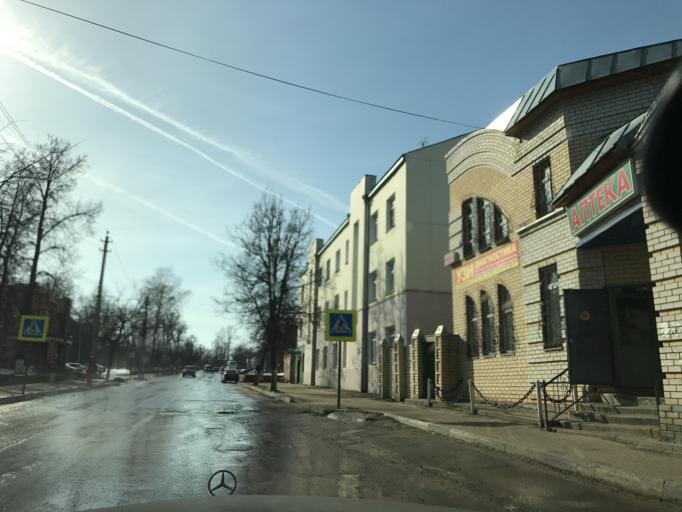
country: RU
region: Nizjnij Novgorod
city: Pavlovo
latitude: 55.9617
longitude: 43.0568
